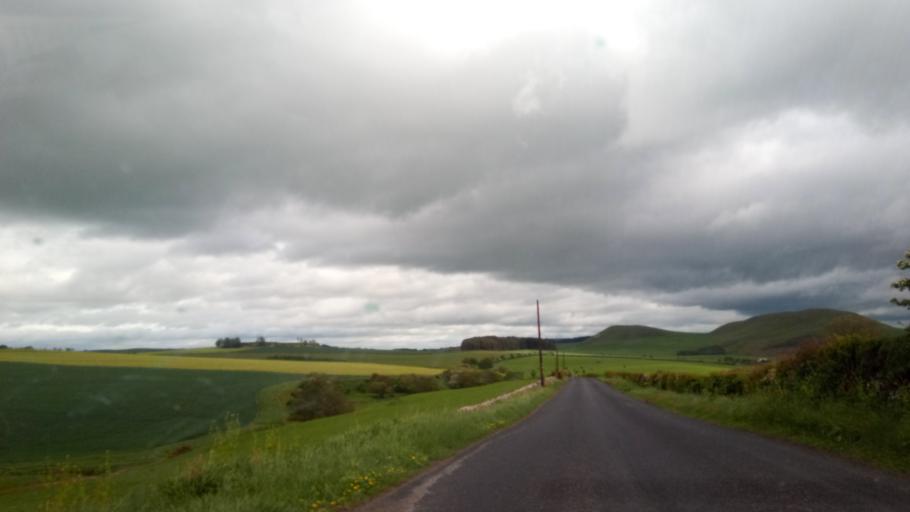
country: GB
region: Scotland
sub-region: The Scottish Borders
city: Hawick
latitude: 55.4712
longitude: -2.7343
